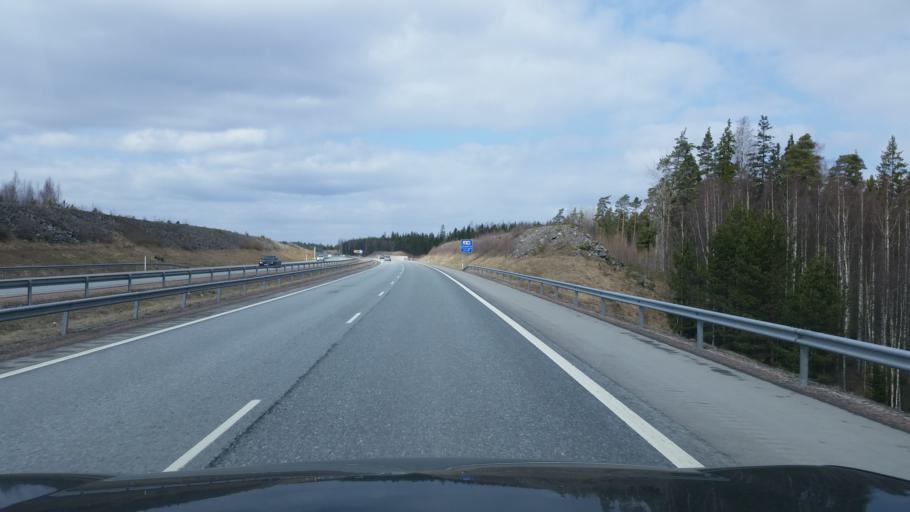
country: FI
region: Uusimaa
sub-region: Helsinki
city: Sammatti
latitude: 60.3637
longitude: 23.8807
